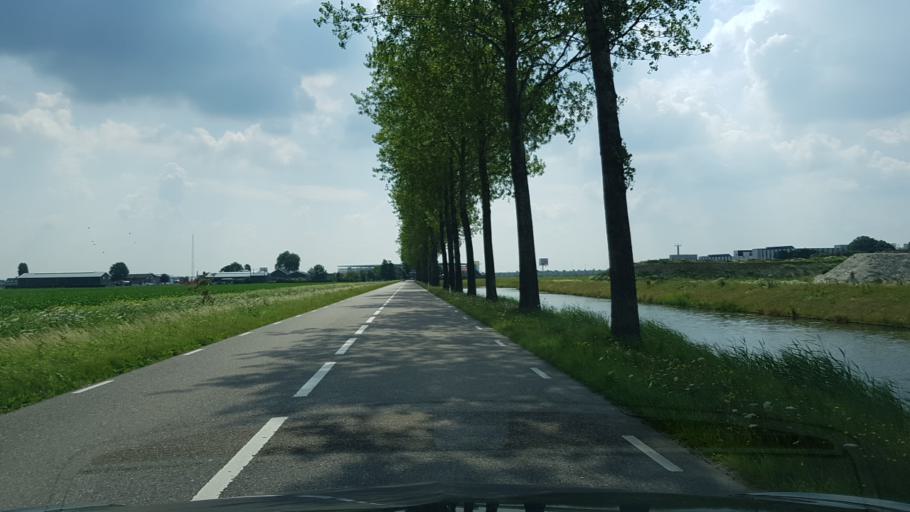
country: NL
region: North Holland
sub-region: Gemeente Aalsmeer
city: Aalsmeer
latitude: 52.3290
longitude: 4.7566
